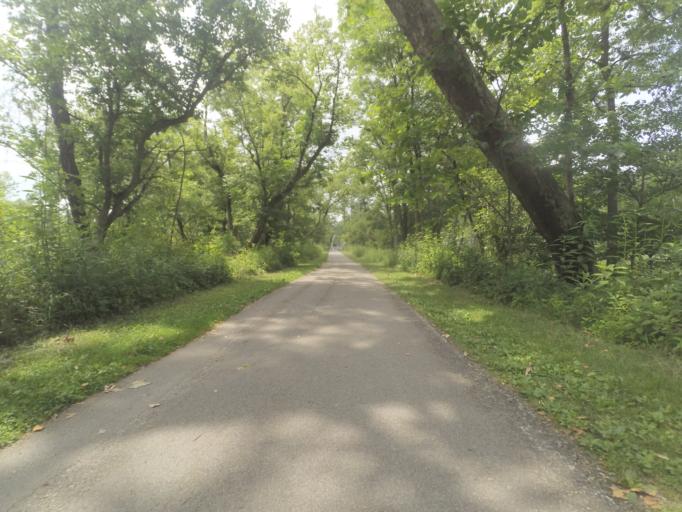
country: US
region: Ohio
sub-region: Cuyahoga County
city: Brecksville
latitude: 41.3199
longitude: -81.5862
